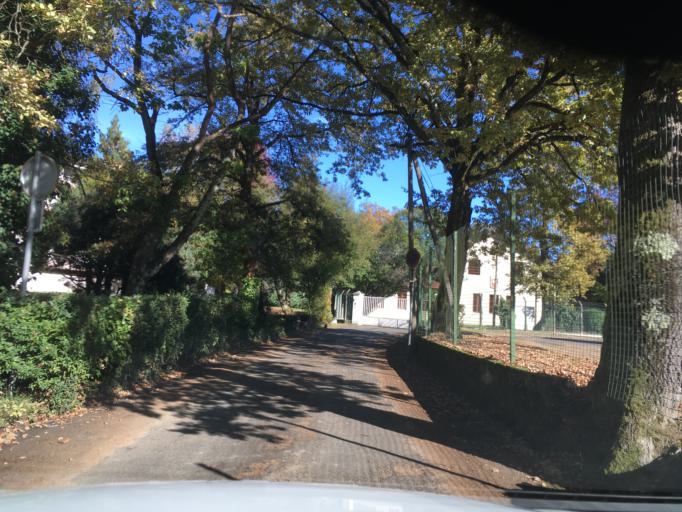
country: FR
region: Aquitaine
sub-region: Departement des Pyrenees-Atlantiques
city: Pau
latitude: 43.3090
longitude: -0.3519
